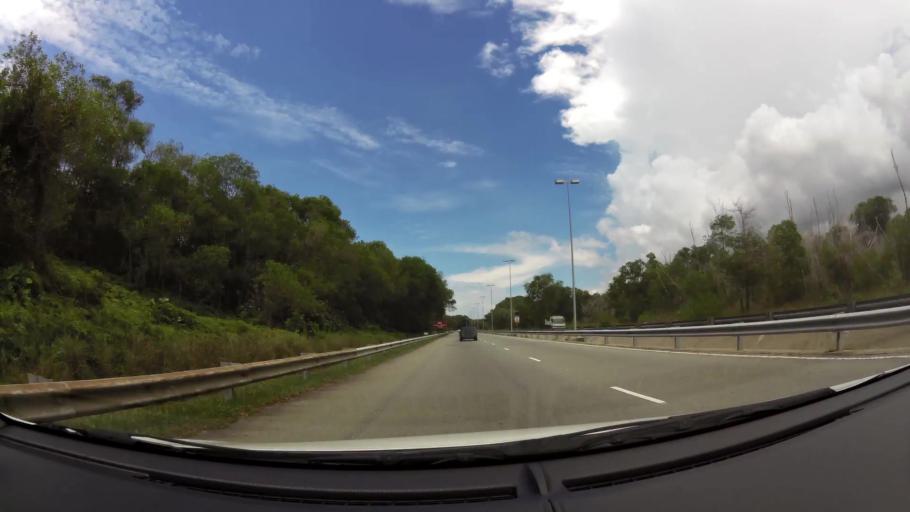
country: BN
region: Brunei and Muara
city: Bandar Seri Begawan
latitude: 4.9864
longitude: 114.9128
